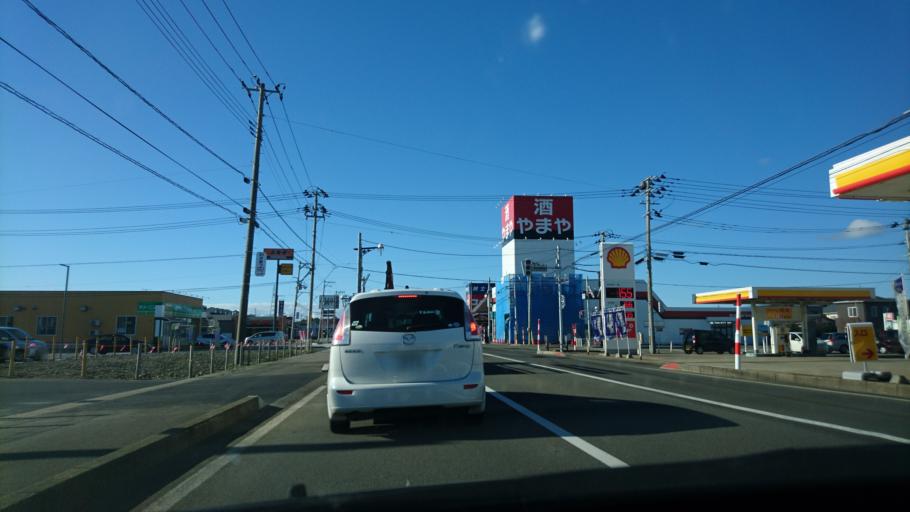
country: JP
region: Akita
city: Akita Shi
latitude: 39.3786
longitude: 140.0596
